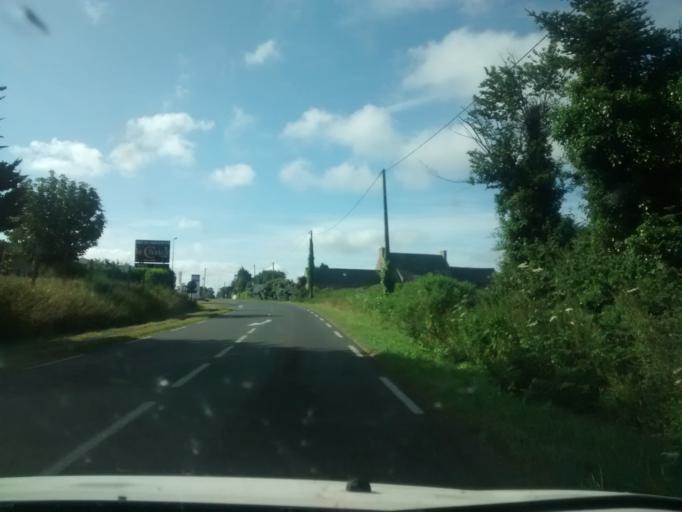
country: FR
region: Brittany
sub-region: Departement des Cotes-d'Armor
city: Louannec
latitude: 48.7880
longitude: -3.3998
